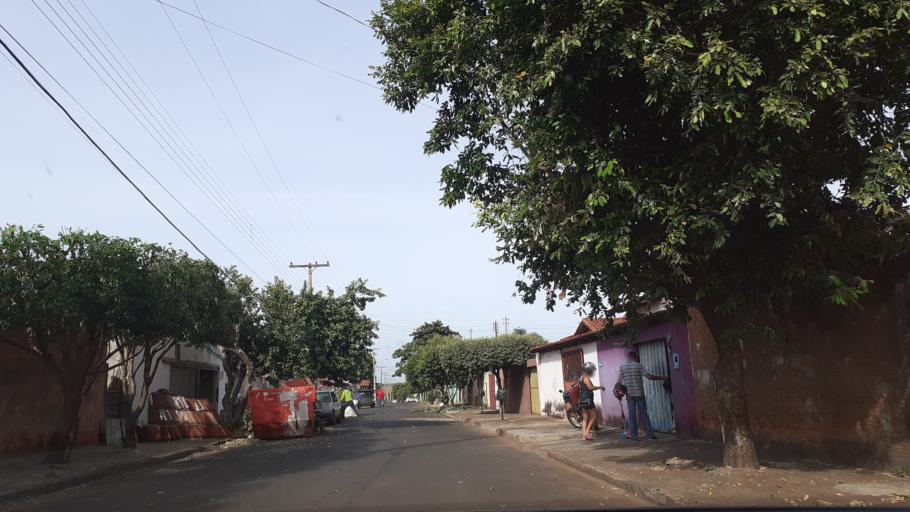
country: BR
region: Goias
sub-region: Itumbiara
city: Itumbiara
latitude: -18.4211
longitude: -49.2478
